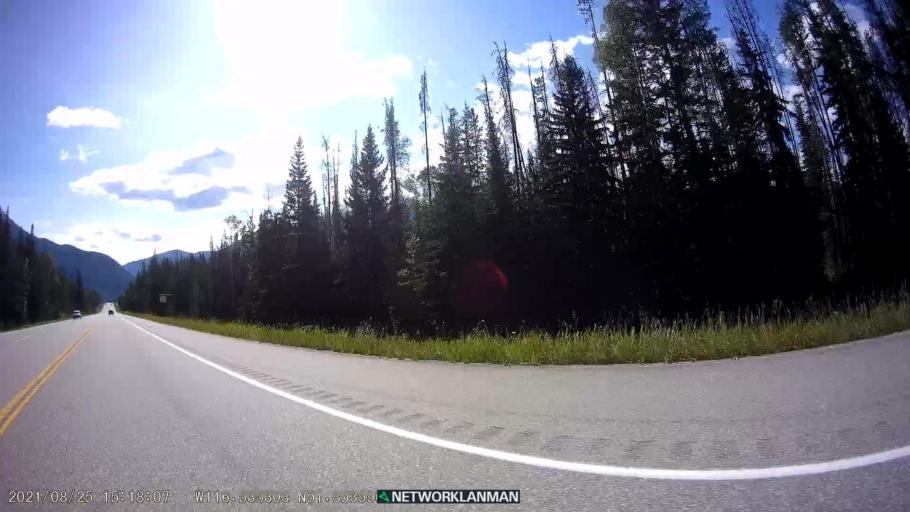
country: CA
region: Alberta
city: Lake Louise
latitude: 51.3540
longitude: -116.5354
